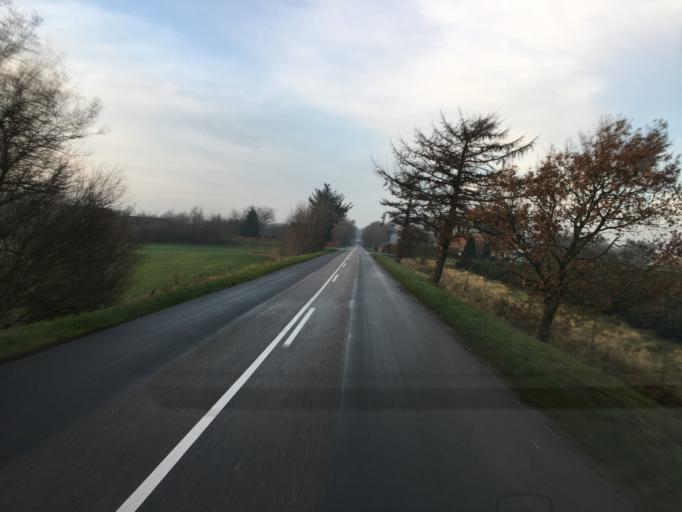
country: DK
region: South Denmark
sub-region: Tonder Kommune
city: Toftlund
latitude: 55.1366
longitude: 9.0607
